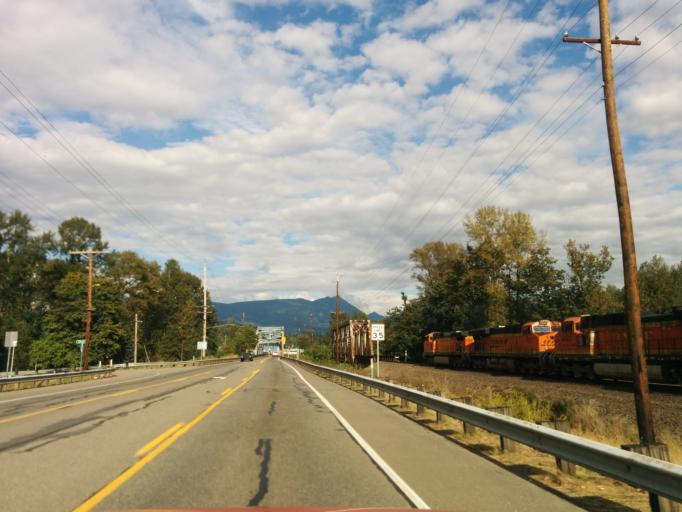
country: US
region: Washington
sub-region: Snohomish County
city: Sultan
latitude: 47.8599
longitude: -121.8236
